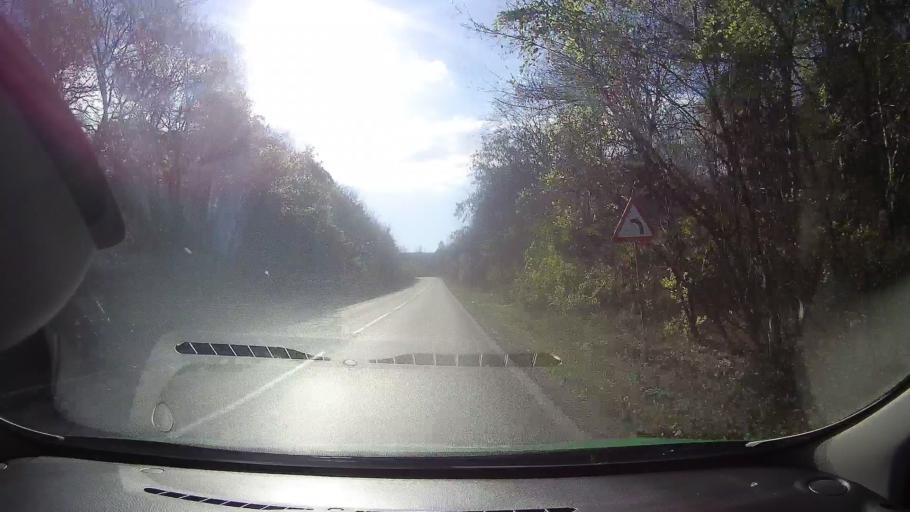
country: RO
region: Tulcea
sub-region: Oras Babadag
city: Babadag
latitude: 44.8722
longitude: 28.6886
